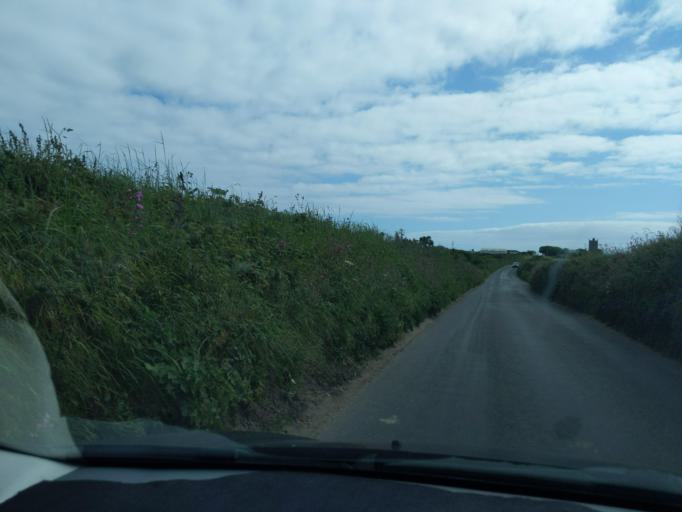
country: GB
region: England
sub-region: Cornwall
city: St. Buryan
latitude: 50.0803
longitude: -5.6174
